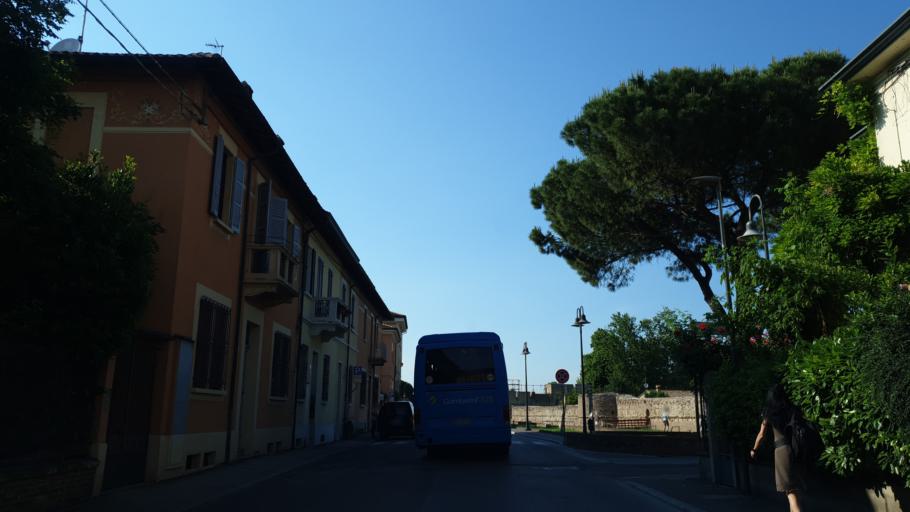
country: IT
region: Emilia-Romagna
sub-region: Provincia di Ravenna
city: Ravenna
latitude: 44.4207
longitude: 12.2054
